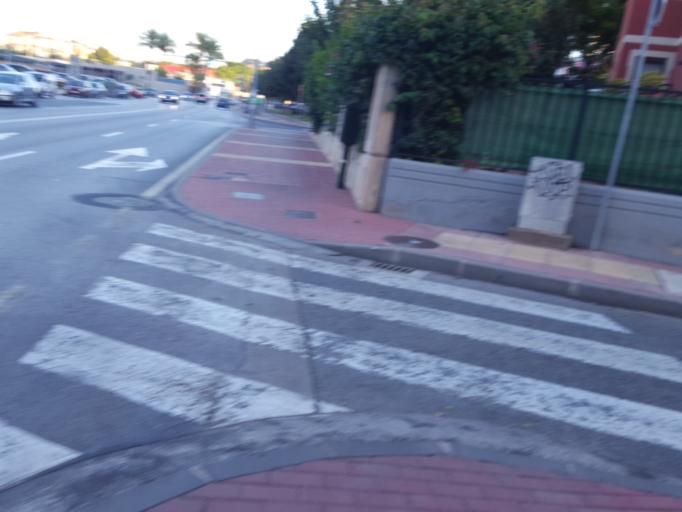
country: ES
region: Murcia
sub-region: Murcia
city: Murcia
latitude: 38.0025
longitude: -1.1459
